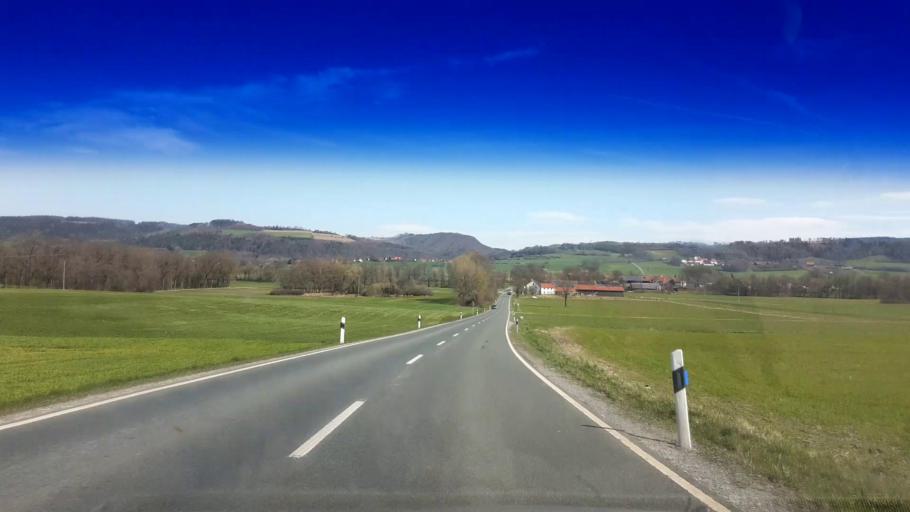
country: DE
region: Bavaria
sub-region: Upper Franconia
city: Gesees
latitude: 50.0196
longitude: 11.6357
